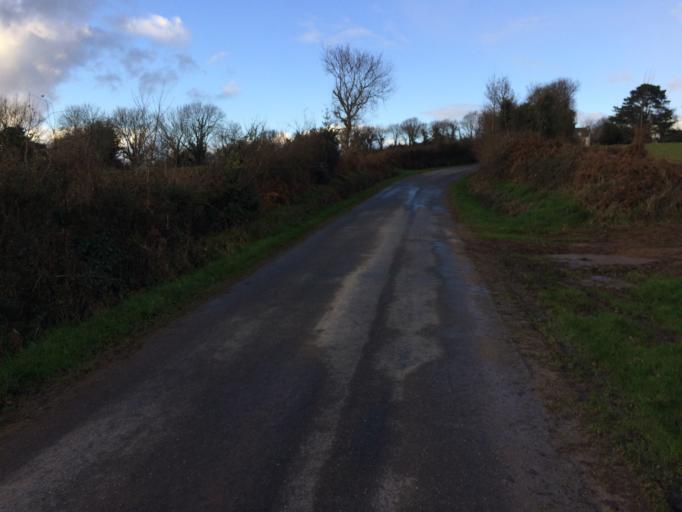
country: FR
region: Brittany
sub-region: Departement du Finistere
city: Hopital-Camfrout
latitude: 48.3321
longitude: -4.2693
